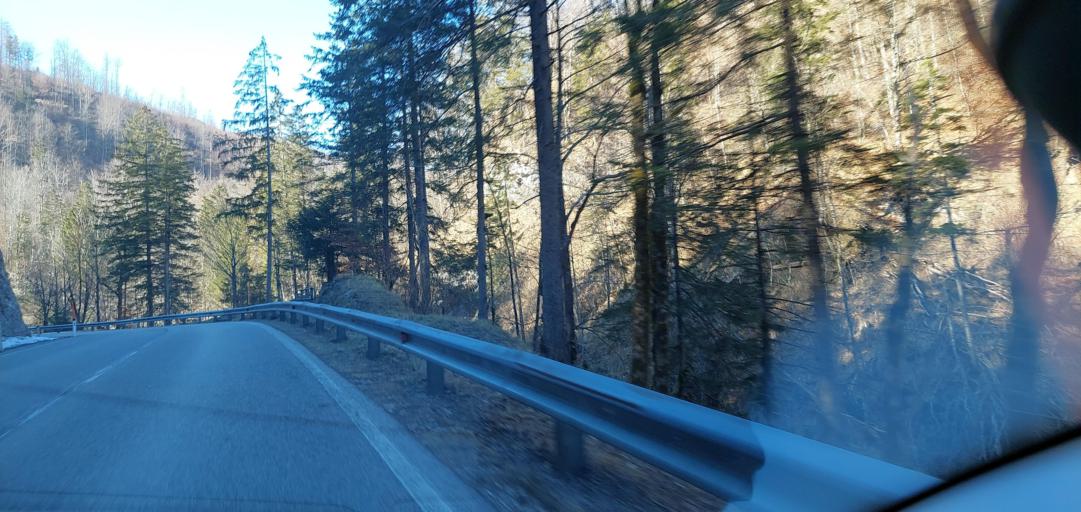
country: AT
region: Upper Austria
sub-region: Politischer Bezirk Gmunden
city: Bad Ischl
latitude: 47.7477
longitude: 13.6619
